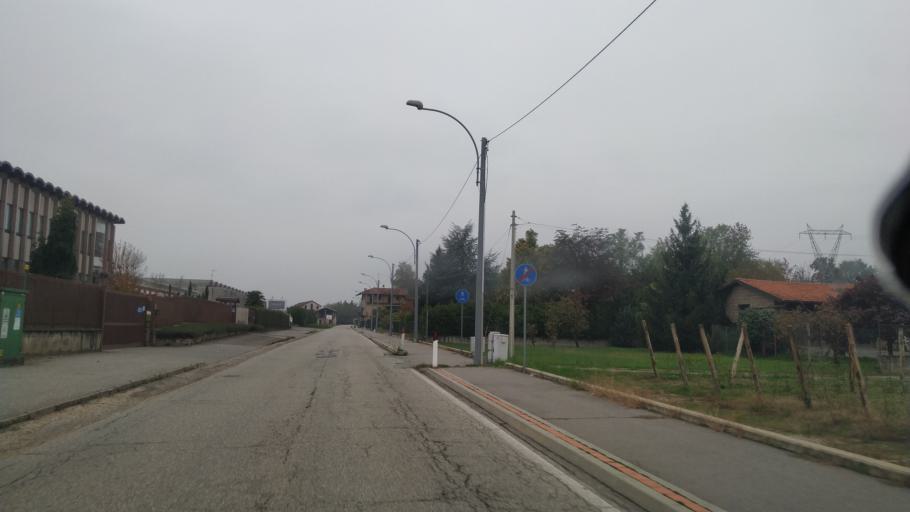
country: IT
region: Piedmont
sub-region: Provincia di Biella
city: Lessona
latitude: 45.5724
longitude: 8.2074
